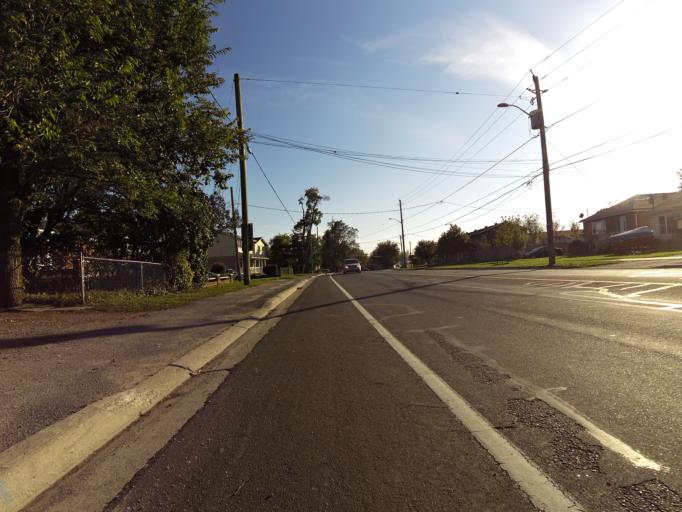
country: CA
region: Ontario
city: Kingston
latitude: 44.2646
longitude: -76.4784
